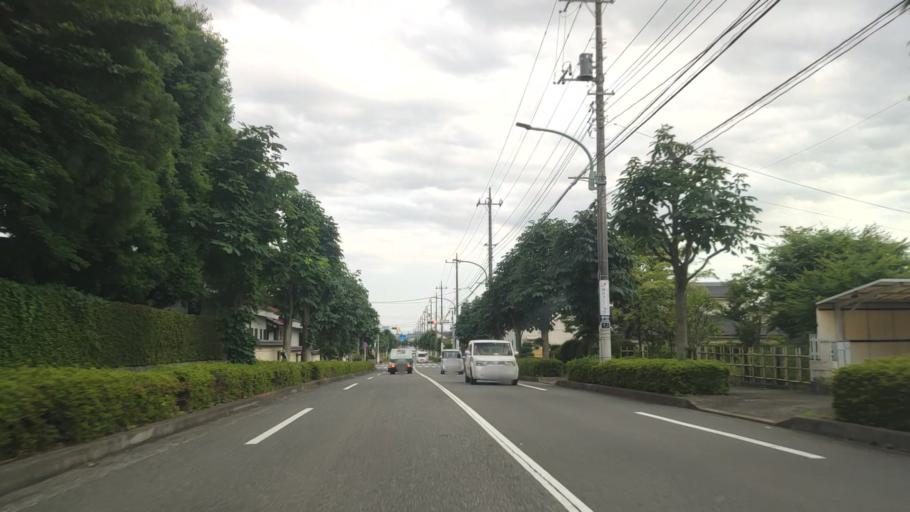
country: JP
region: Tokyo
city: Ome
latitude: 35.7905
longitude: 139.2990
